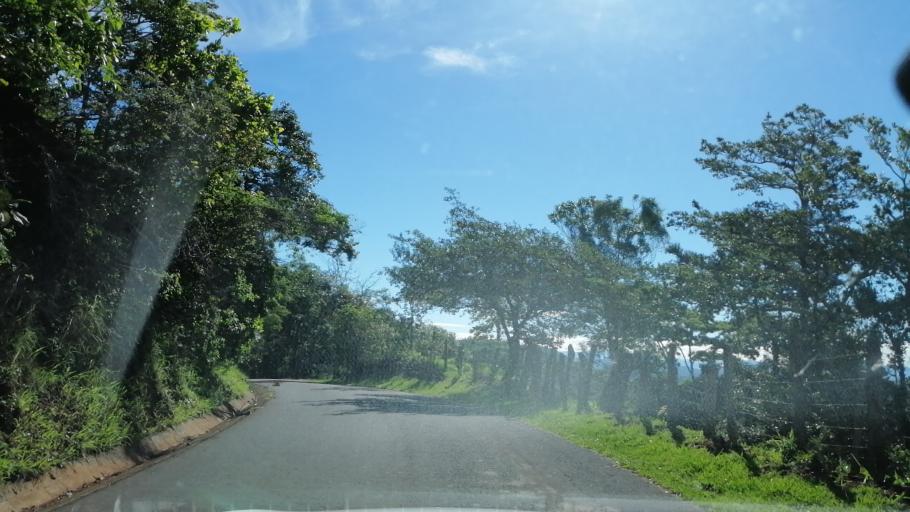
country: SV
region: Morazan
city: Corinto
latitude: 13.8105
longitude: -87.9928
